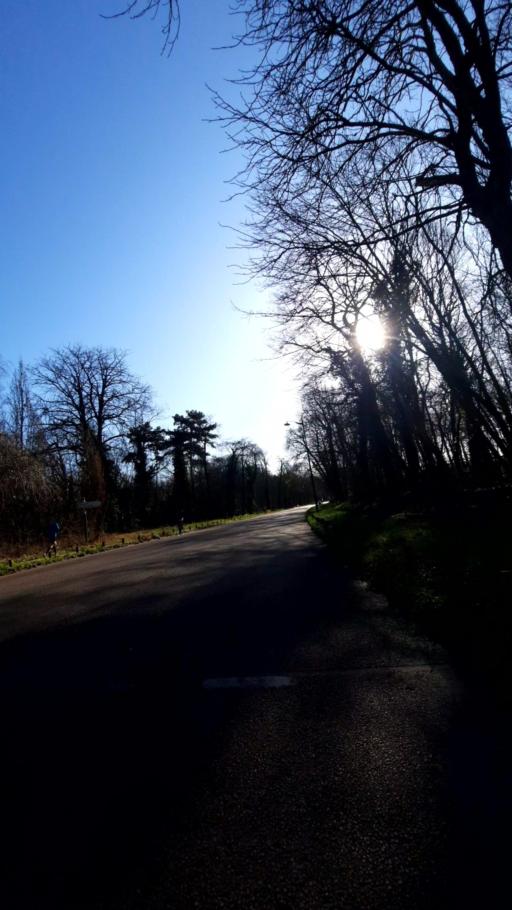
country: FR
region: Ile-de-France
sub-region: Departement du Val-de-Marne
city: Saint-Maurice
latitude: 48.8228
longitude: 2.4314
